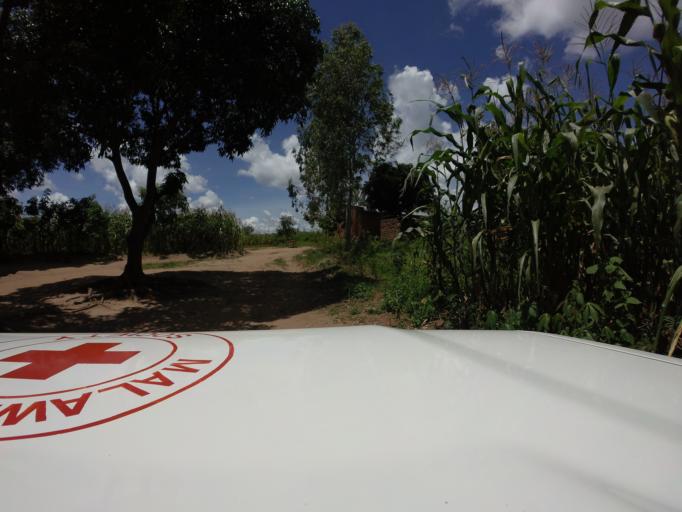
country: MW
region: Southern Region
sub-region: Thyolo District
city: Thyolo
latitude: -15.9542
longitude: 35.1578
